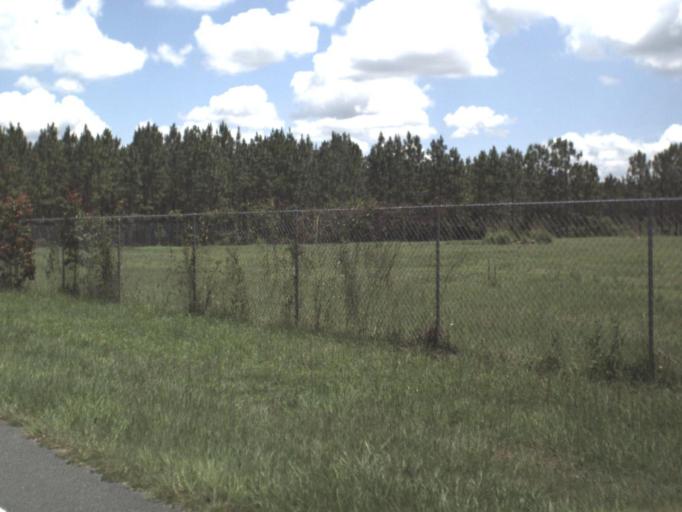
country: US
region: Florida
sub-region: Alachua County
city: Hawthorne
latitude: 29.6168
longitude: -82.0264
